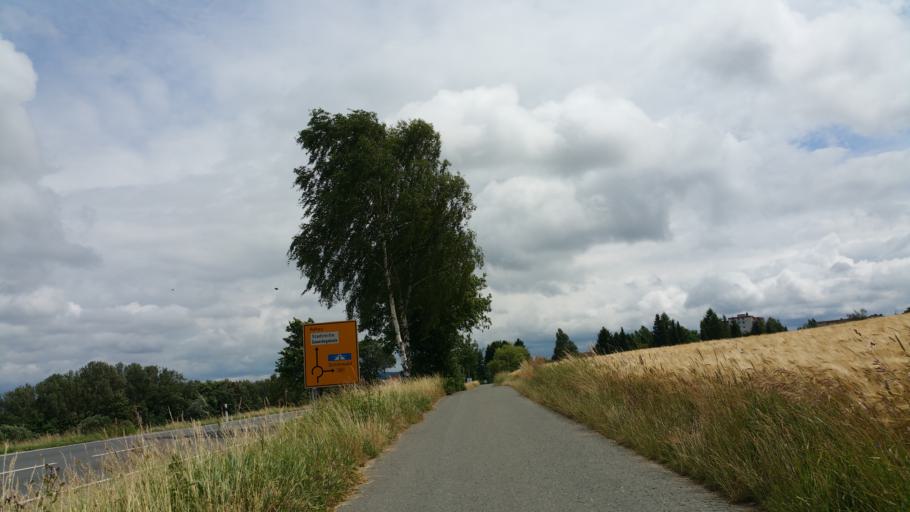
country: DE
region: Bavaria
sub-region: Upper Franconia
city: Rehau
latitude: 50.2437
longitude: 12.0139
